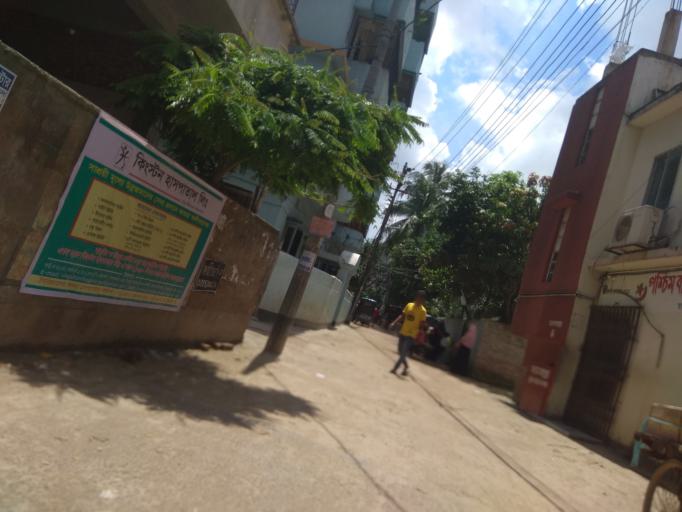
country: BD
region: Dhaka
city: Tungi
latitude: 23.8309
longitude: 90.3842
